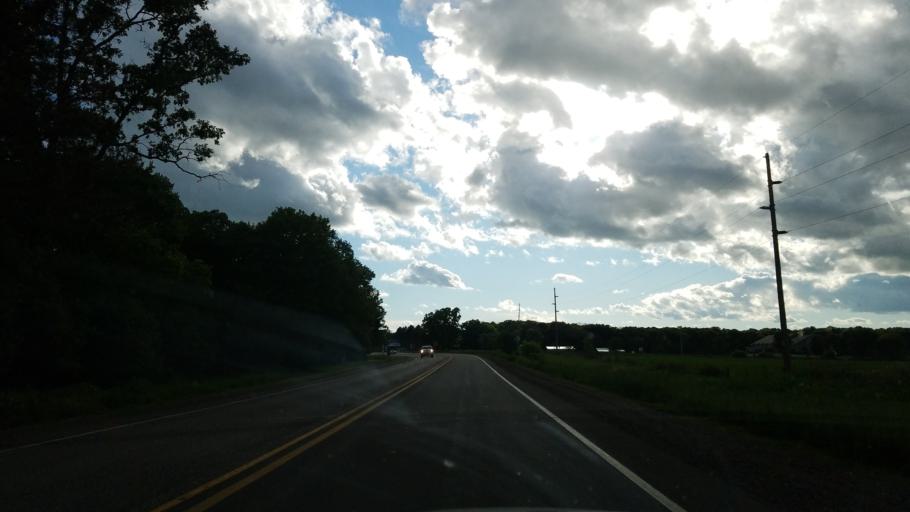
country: US
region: Wisconsin
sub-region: Polk County
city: Osceola
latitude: 45.3433
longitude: -92.6638
